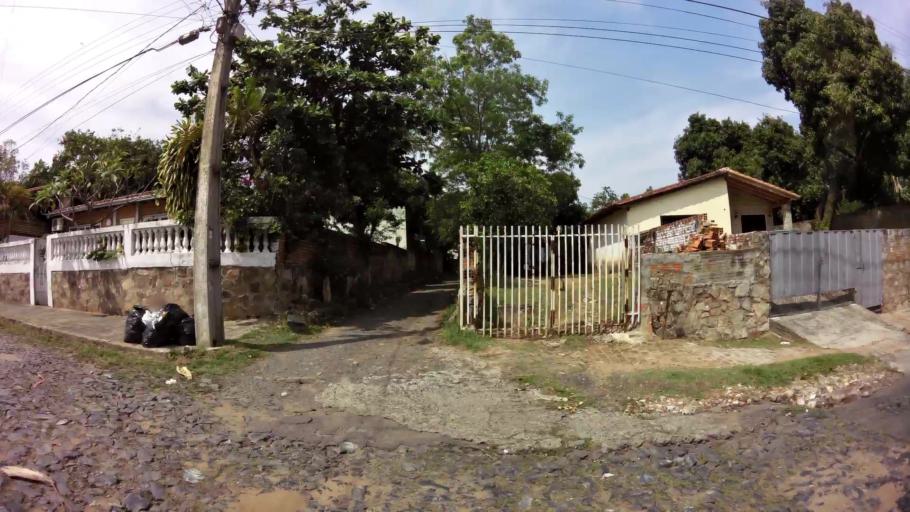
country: PY
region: Asuncion
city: Asuncion
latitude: -25.2652
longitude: -57.5836
